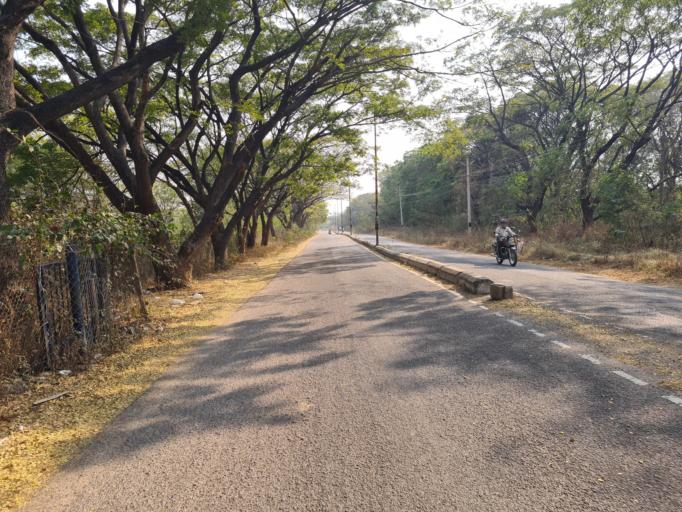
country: IN
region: Telangana
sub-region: Medak
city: Serilingampalle
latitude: 17.4887
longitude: 78.2979
